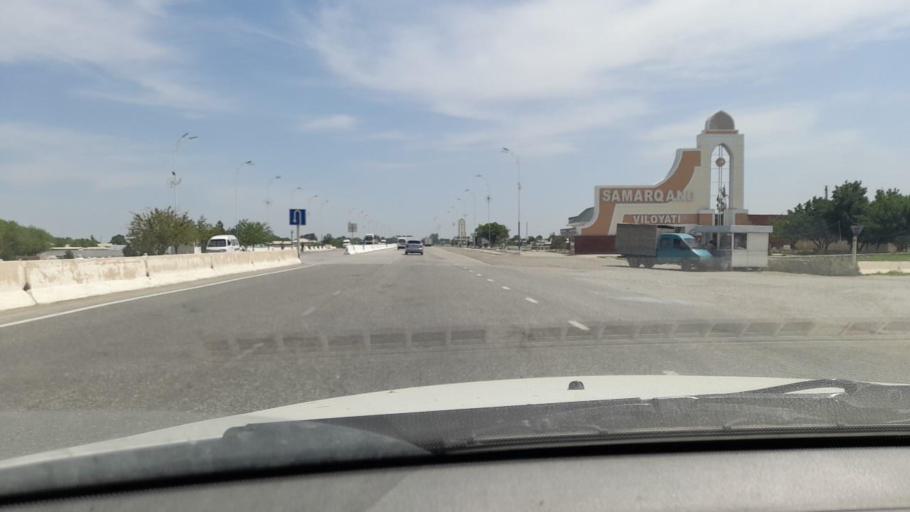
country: UZ
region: Navoiy
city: Navoiy
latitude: 40.1184
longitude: 65.4900
